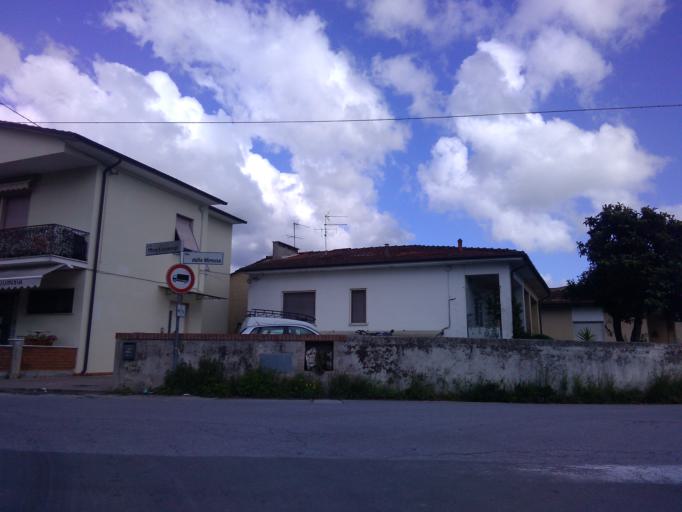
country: IT
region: Tuscany
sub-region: Provincia di Lucca
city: Strettoia
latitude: 43.9860
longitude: 10.1886
